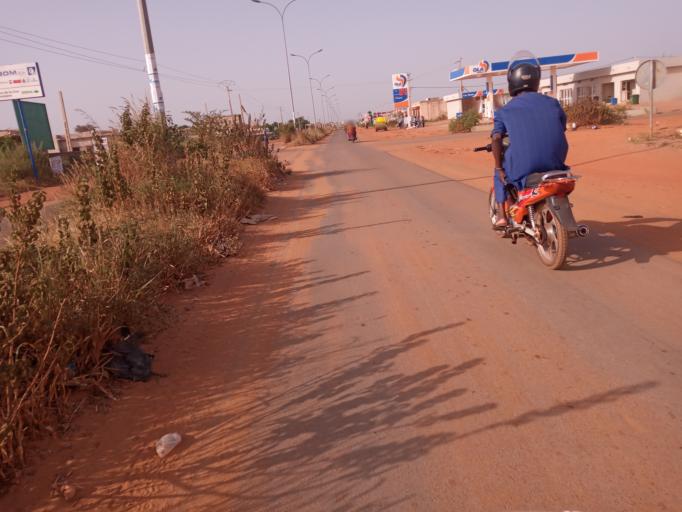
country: ML
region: Bamako
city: Bamako
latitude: 12.4887
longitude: -8.0565
